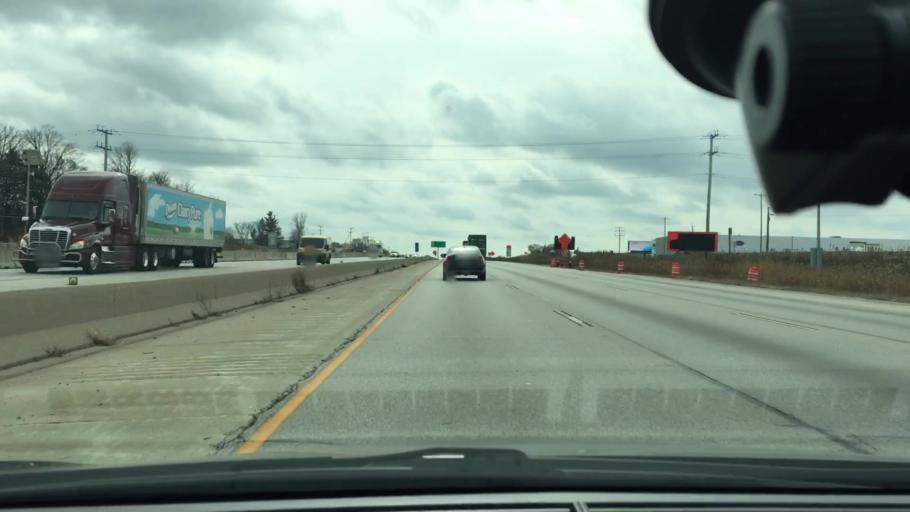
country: US
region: Wisconsin
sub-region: Racine County
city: Caledonia
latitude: 42.8230
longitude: -87.9528
